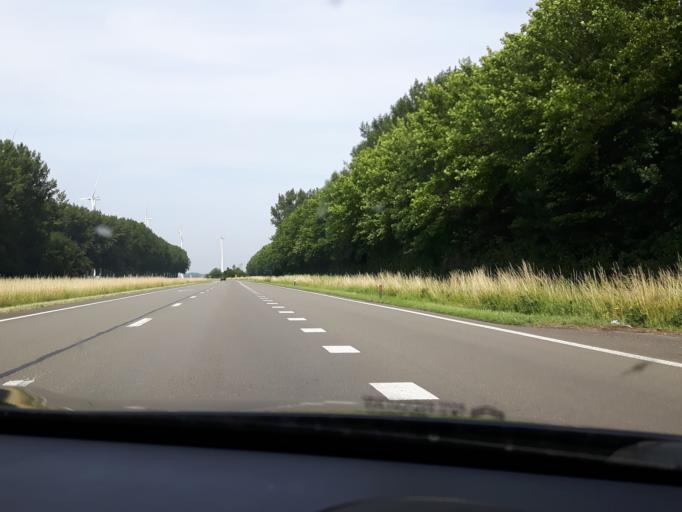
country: NL
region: Zeeland
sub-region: Gemeente Borsele
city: Borssele
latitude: 51.4758
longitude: 3.6836
